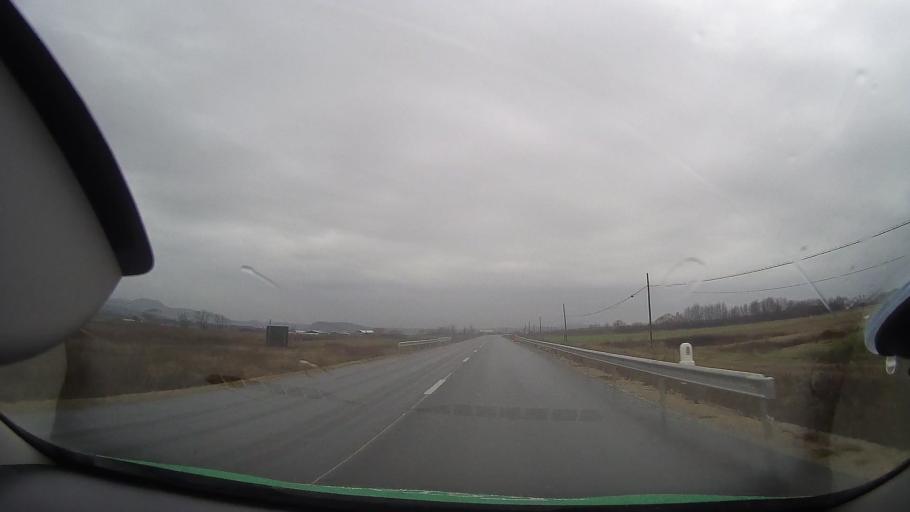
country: RO
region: Bihor
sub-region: Municipiul Beius
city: Beius
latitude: 46.6732
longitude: 22.3277
